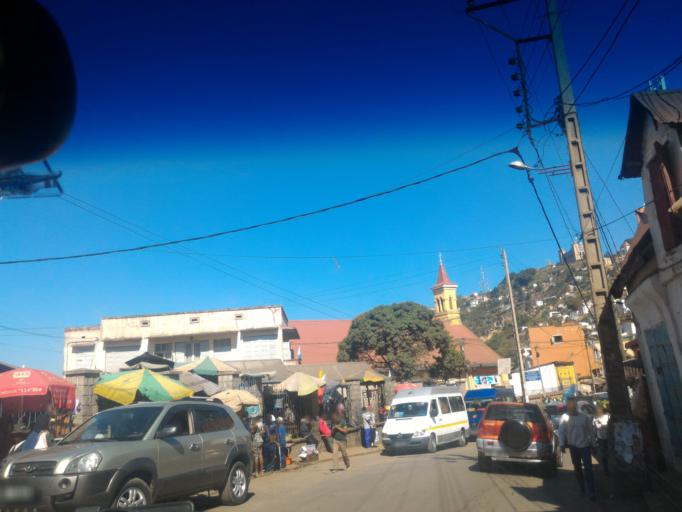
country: MG
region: Analamanga
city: Antananarivo
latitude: -18.9191
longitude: 47.5385
